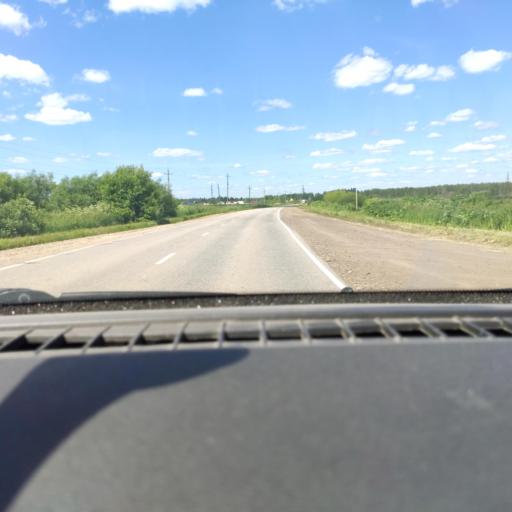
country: RU
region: Perm
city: Ust'-Kachka
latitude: 58.0759
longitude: 55.6199
